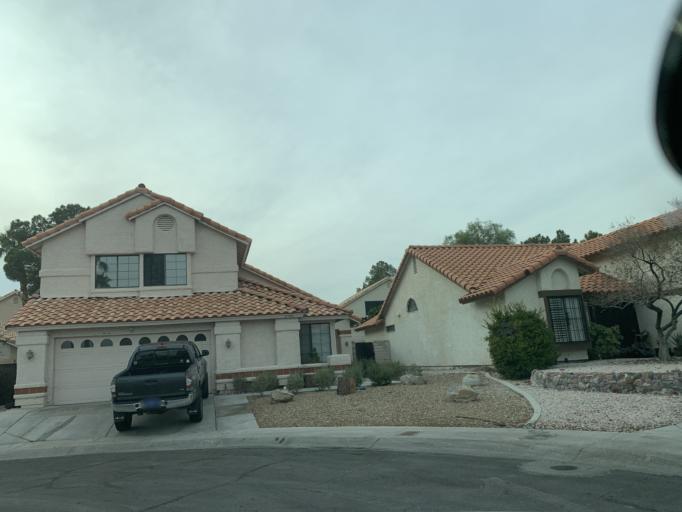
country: US
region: Nevada
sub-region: Clark County
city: Summerlin South
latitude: 36.1427
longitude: -115.2959
